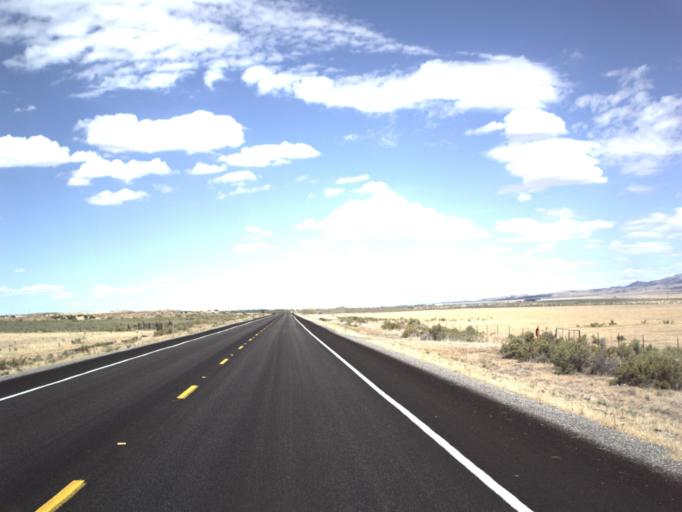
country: US
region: Utah
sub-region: Millard County
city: Fillmore
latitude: 39.1260
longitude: -112.3587
